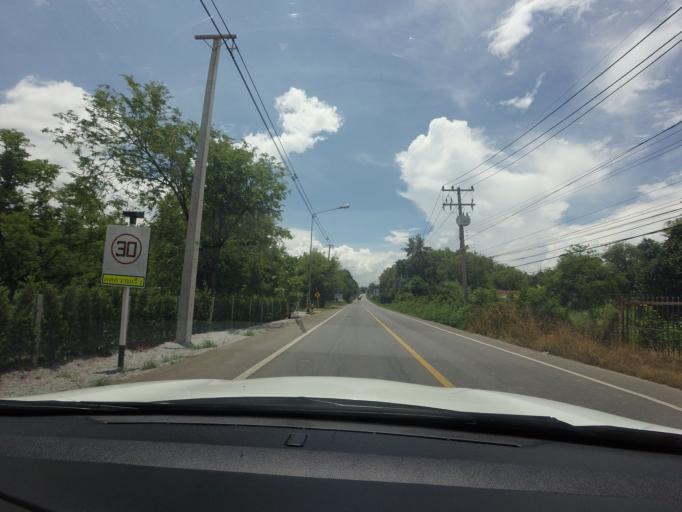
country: TH
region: Sara Buri
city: Muak Lek
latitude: 14.6009
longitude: 101.2146
